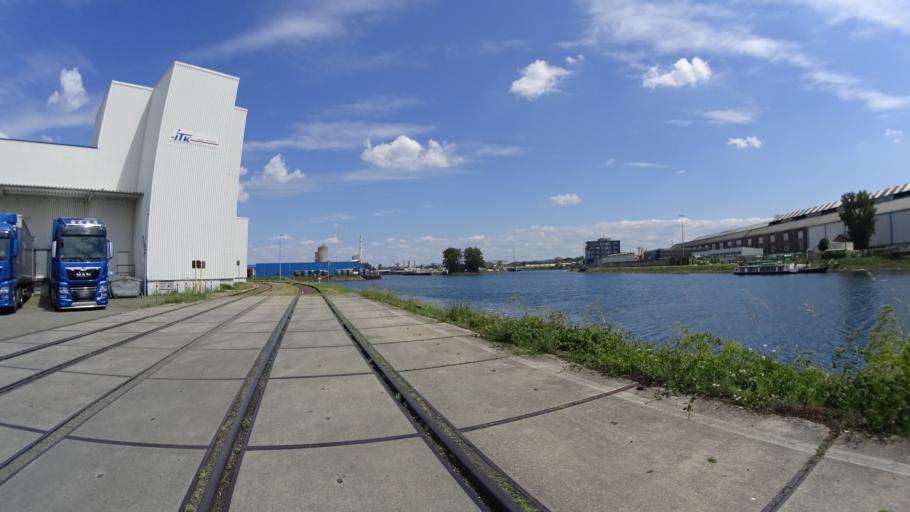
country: DE
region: Baden-Wuerttemberg
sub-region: Karlsruhe Region
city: Rheinstetten
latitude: 49.0164
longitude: 8.3274
